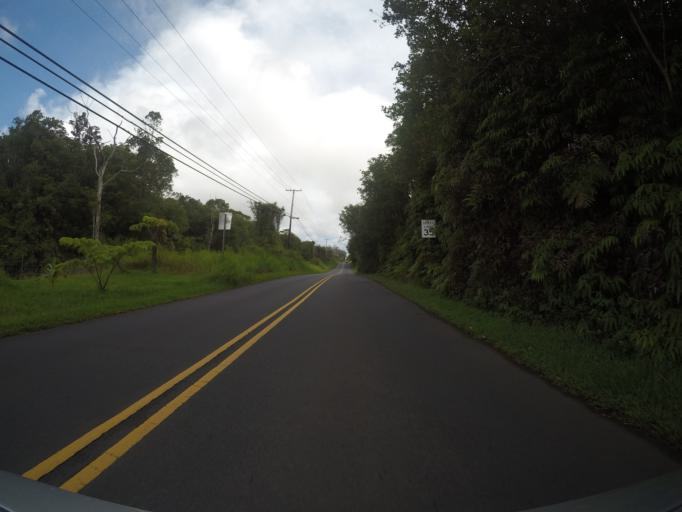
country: US
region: Hawaii
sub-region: Hawaii County
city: Fern Acres
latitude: 19.4830
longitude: -155.1477
